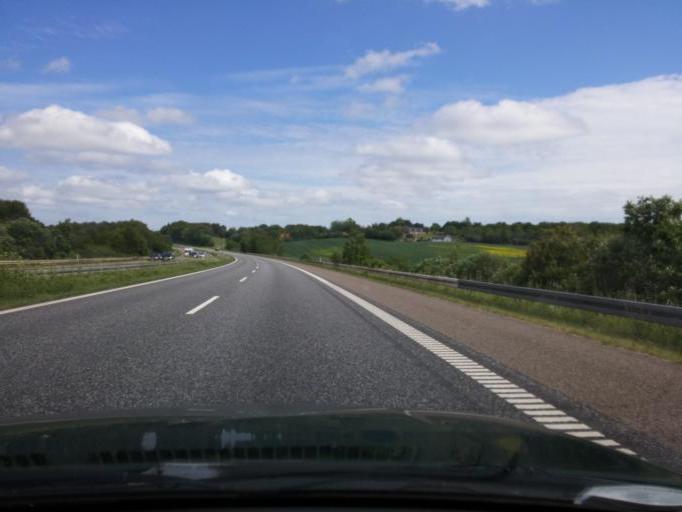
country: DK
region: South Denmark
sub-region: Fredericia Kommune
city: Taulov
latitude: 55.5428
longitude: 9.5921
